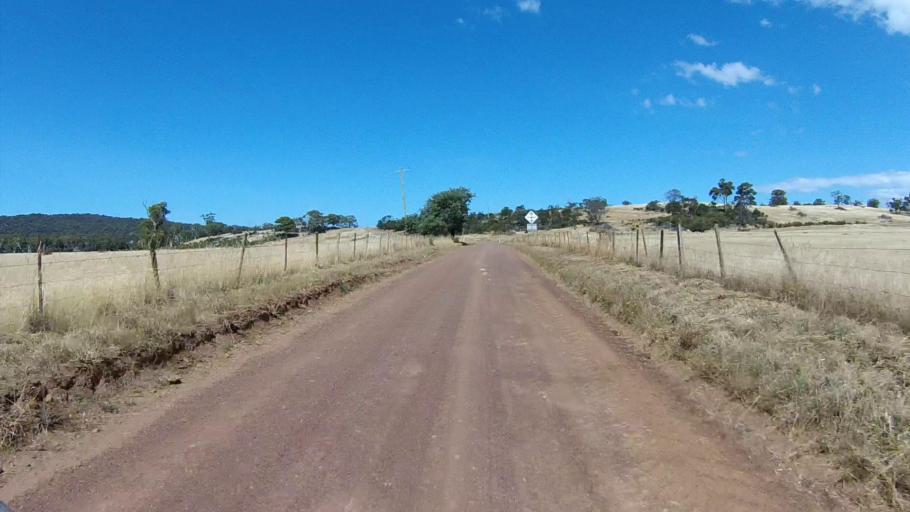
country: AU
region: Tasmania
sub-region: Break O'Day
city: St Helens
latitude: -41.9631
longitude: 148.0729
